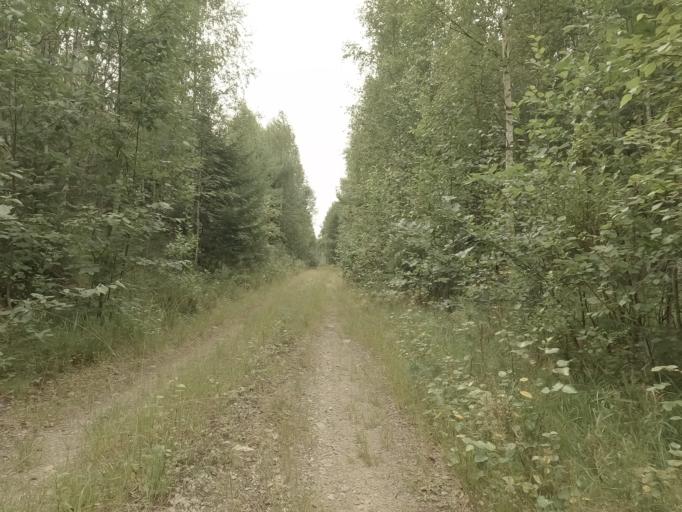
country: RU
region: Leningrad
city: Kamennogorsk
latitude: 61.0204
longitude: 29.1648
